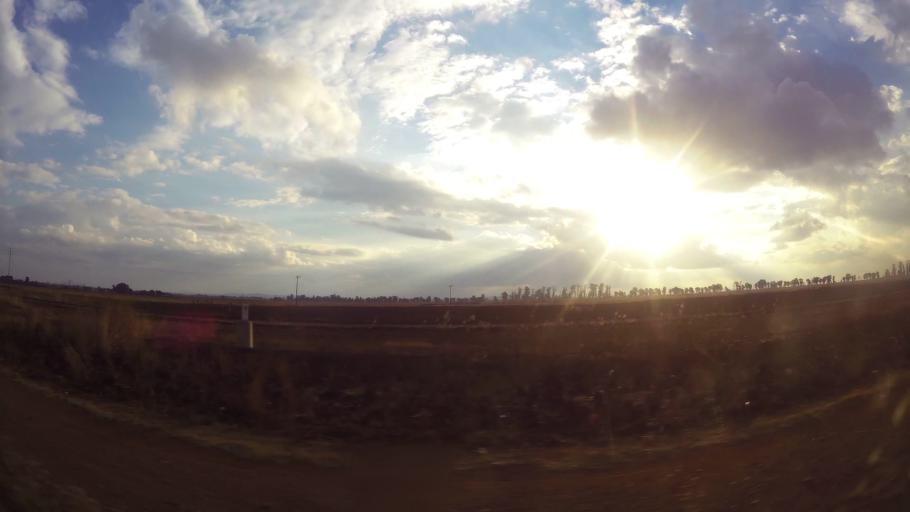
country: ZA
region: Gauteng
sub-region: Sedibeng District Municipality
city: Vanderbijlpark
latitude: -26.6546
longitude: 27.8025
